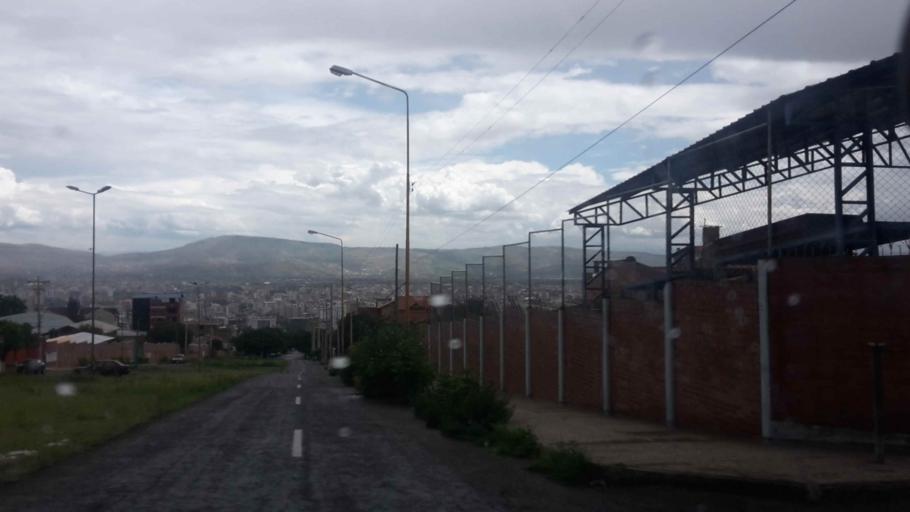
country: BO
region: Cochabamba
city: Cochabamba
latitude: -17.3592
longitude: -66.1586
